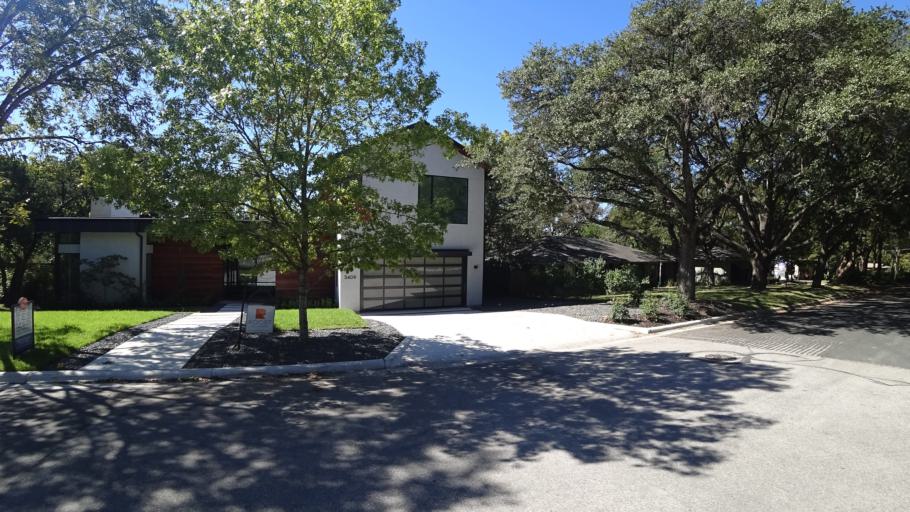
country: US
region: Texas
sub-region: Travis County
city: West Lake Hills
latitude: 30.3164
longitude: -97.7695
